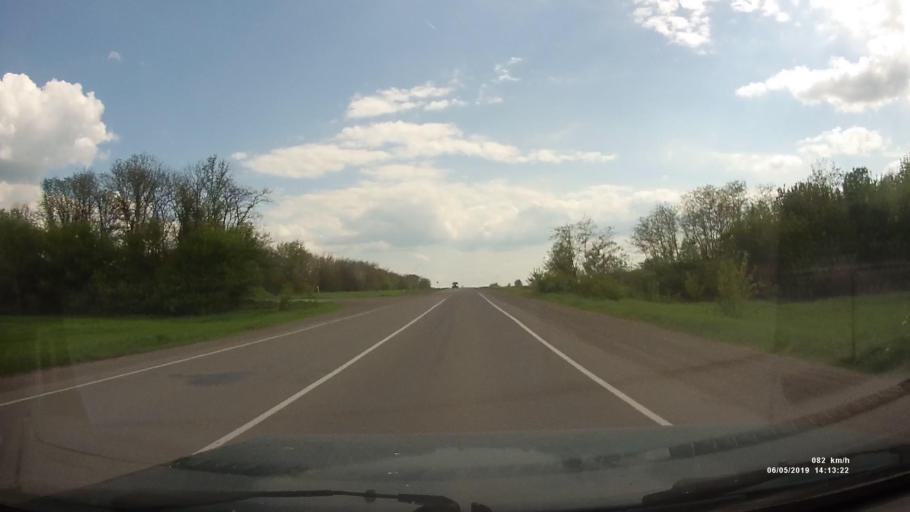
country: RU
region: Rostov
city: Kamenolomni
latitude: 47.6613
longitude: 40.2924
